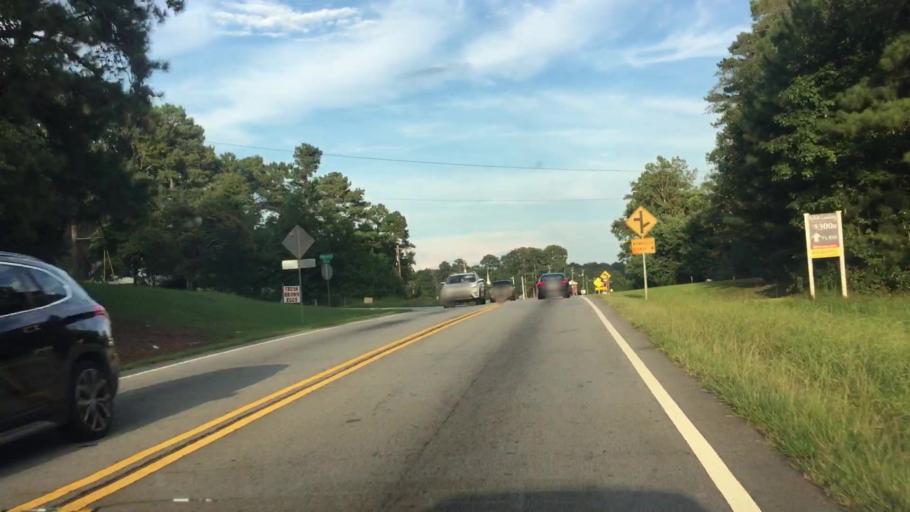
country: US
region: Georgia
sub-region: Henry County
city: Stockbridge
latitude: 33.5404
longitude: -84.1976
